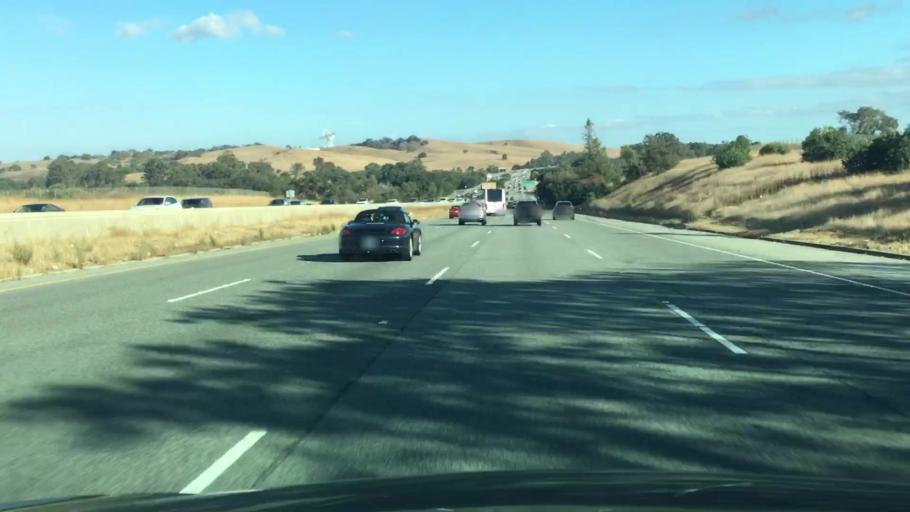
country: US
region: California
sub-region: San Mateo County
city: Ladera
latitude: 37.4120
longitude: -122.2044
